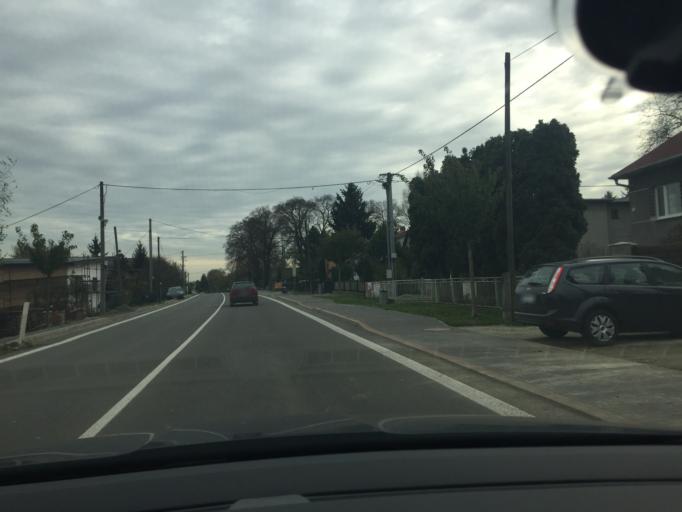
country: SK
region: Kosicky
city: Kosice
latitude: 48.8031
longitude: 21.3023
